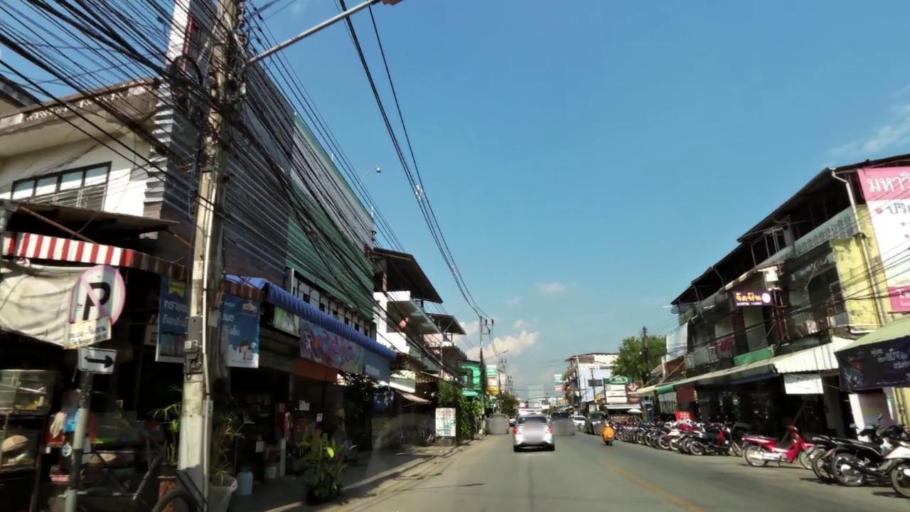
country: TH
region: Chiang Rai
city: Chiang Rai
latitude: 19.9041
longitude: 99.8284
